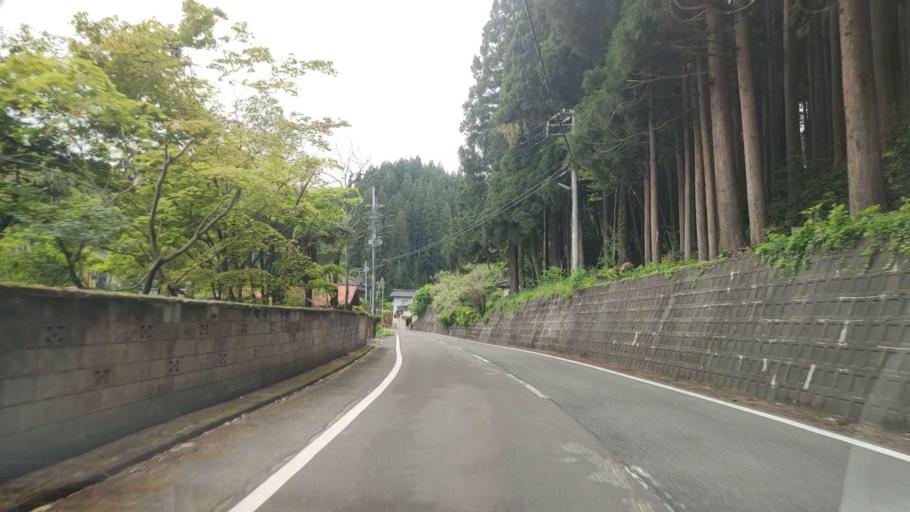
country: JP
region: Niigata
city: Gosen
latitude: 37.7226
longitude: 139.1284
